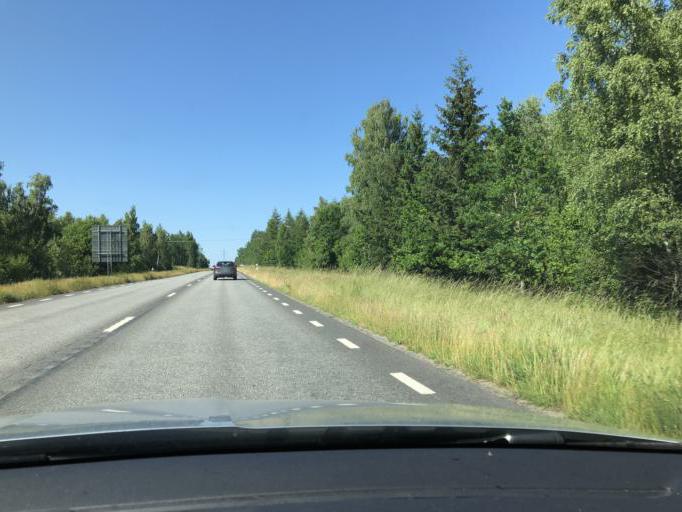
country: SE
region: Skane
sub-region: Bromolla Kommun
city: Bromoella
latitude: 56.0711
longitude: 14.4988
